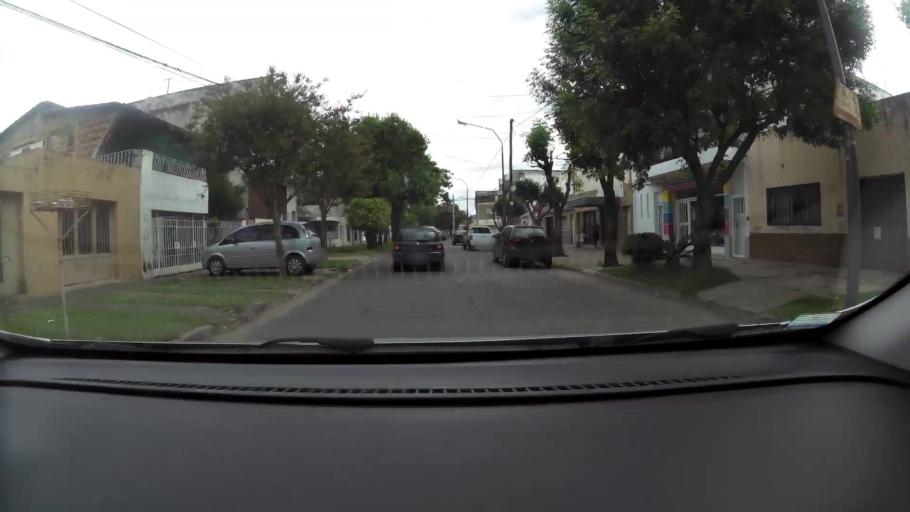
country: AR
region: Santa Fe
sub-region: Departamento de Rosario
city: Rosario
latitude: -32.9805
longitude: -60.6555
